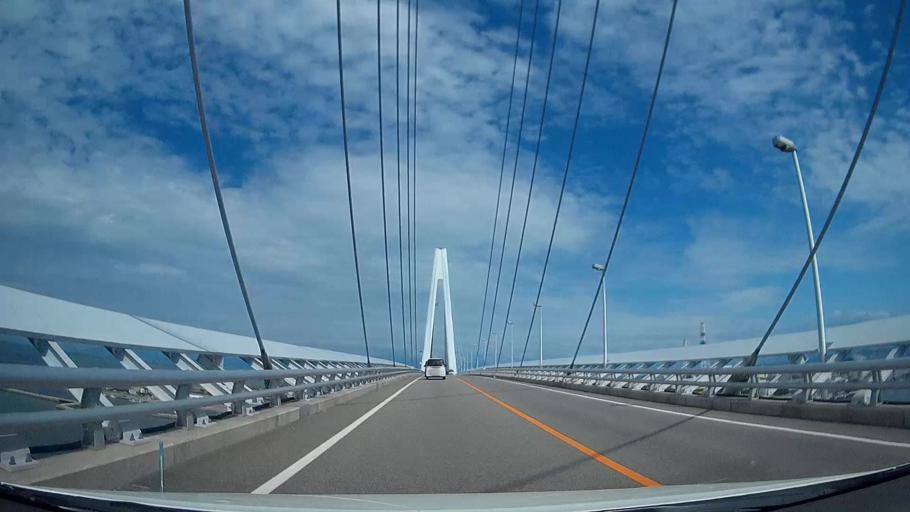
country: JP
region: Toyama
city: Nishishinminato
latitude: 36.7762
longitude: 137.1150
